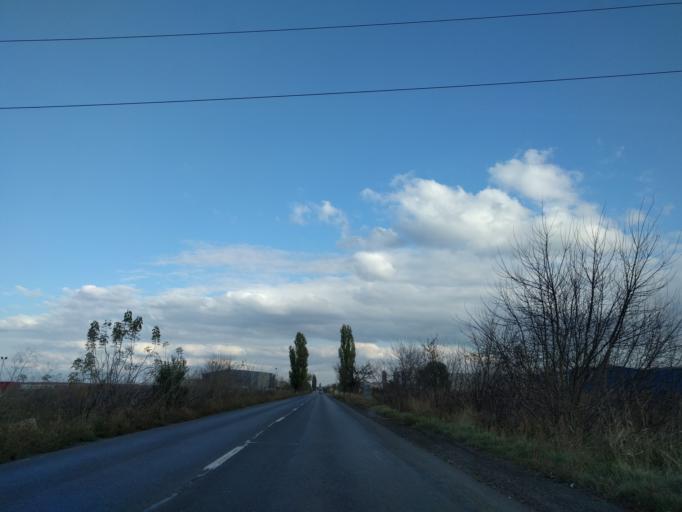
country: RO
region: Ilfov
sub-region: Comuna Cernica
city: Caldararu
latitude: 44.4525
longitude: 26.2520
